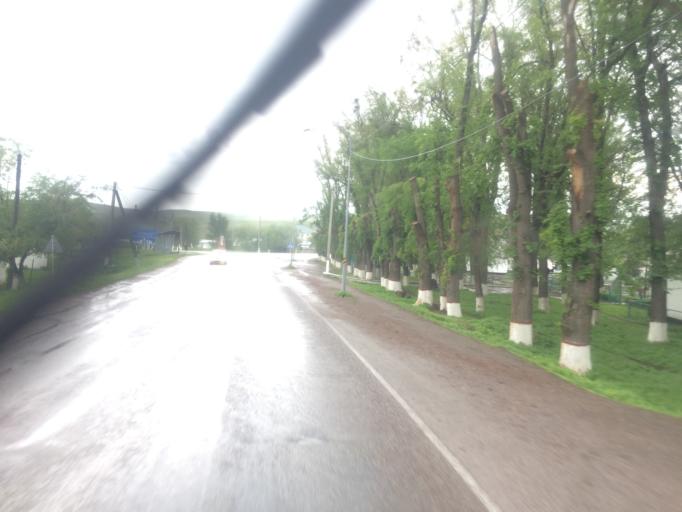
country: KZ
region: Zhambyl
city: Georgiyevka
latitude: 43.2338
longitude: 74.7601
